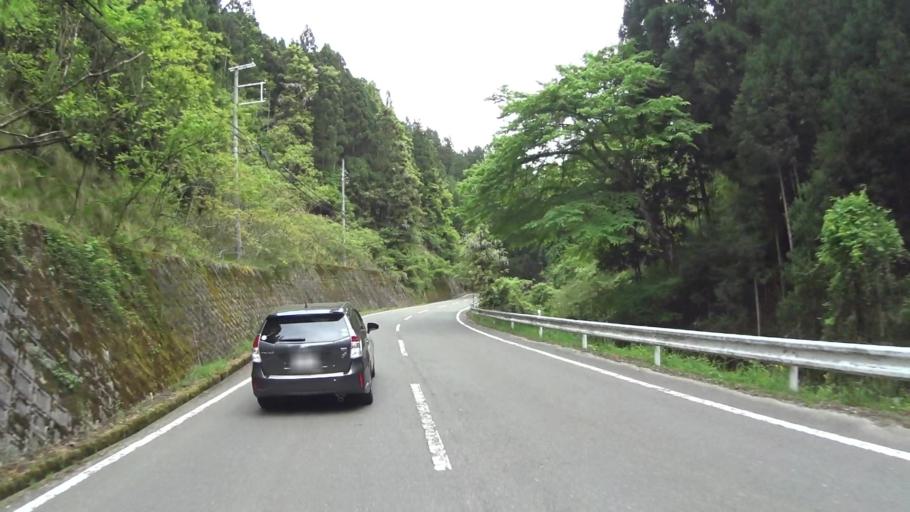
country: JP
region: Kyoto
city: Kameoka
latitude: 35.1371
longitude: 135.6156
